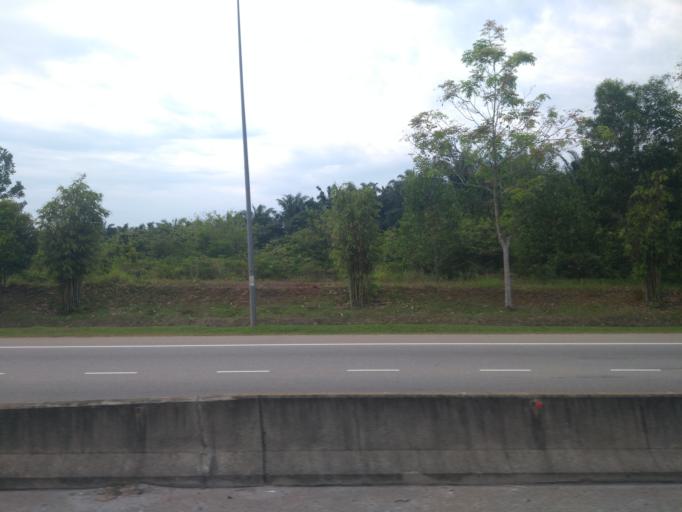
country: MY
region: Melaka
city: Kampung Ayer Keroh
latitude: 2.2866
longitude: 102.2665
